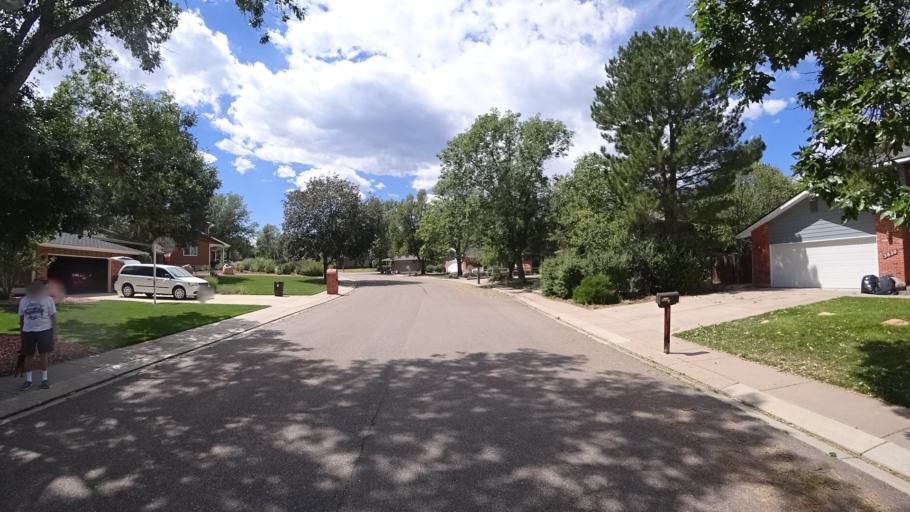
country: US
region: Colorado
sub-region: El Paso County
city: Stratmoor
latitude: 38.7742
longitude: -104.8186
